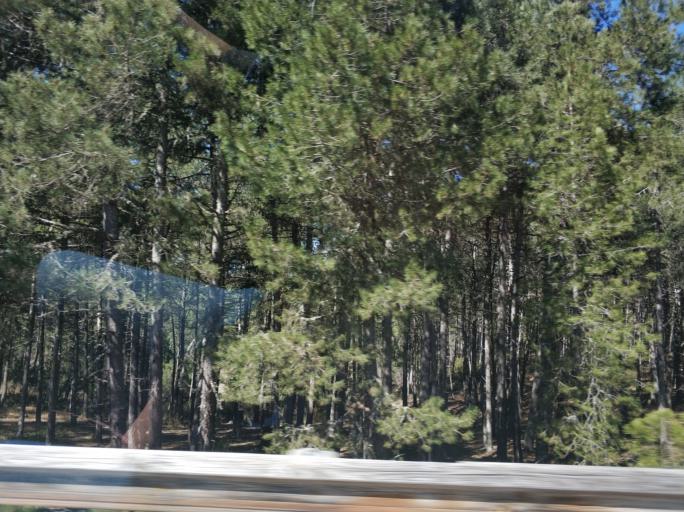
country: ES
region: Castille and Leon
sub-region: Provincia de Soria
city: Herrera de Soria
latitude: 41.7573
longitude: -3.0391
